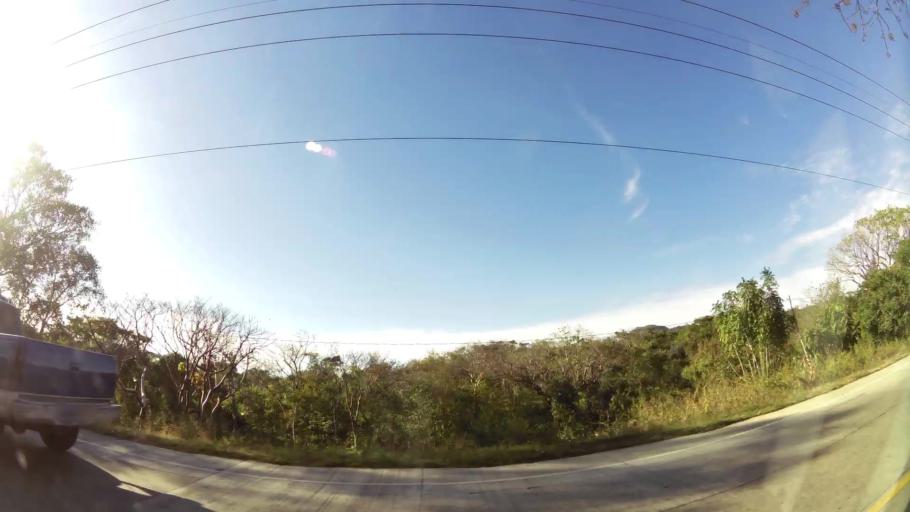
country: SV
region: Santa Ana
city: Metapan
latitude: 14.2472
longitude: -89.4692
